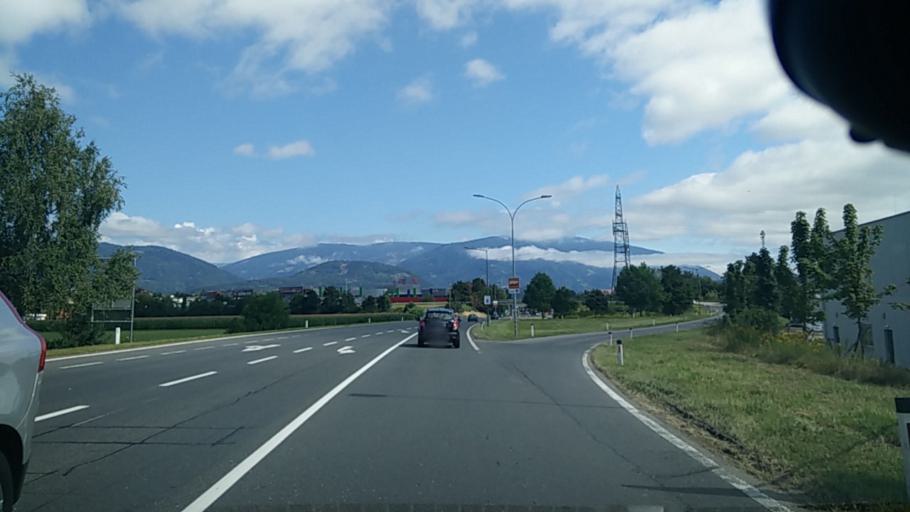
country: AT
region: Carinthia
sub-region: Villach Stadt
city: Villach
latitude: 46.5910
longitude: 13.8341
